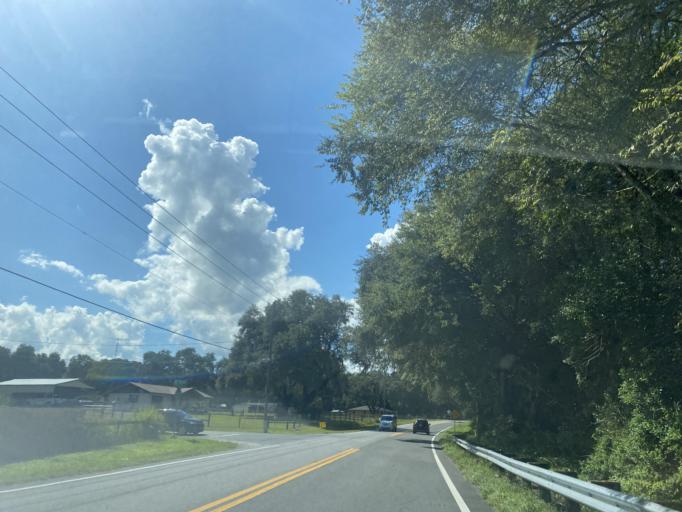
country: US
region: Florida
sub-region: Lake County
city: Lady Lake
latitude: 28.9829
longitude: -81.8956
